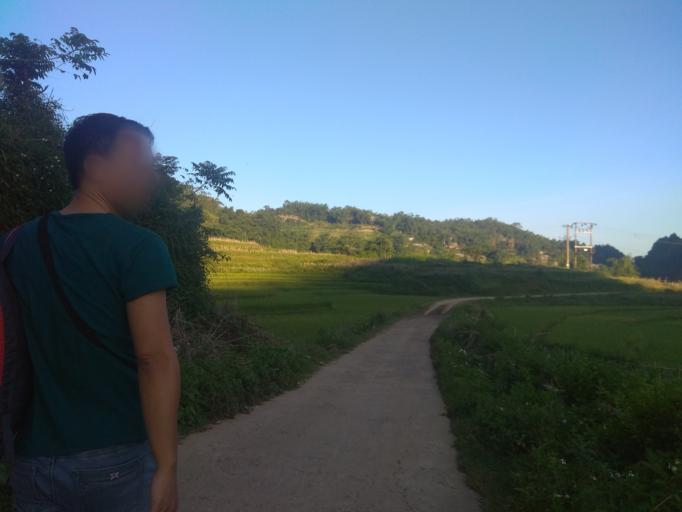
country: VN
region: Hoa Binh
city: Thi Tran Muong Khen
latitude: 20.5604
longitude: 105.1803
